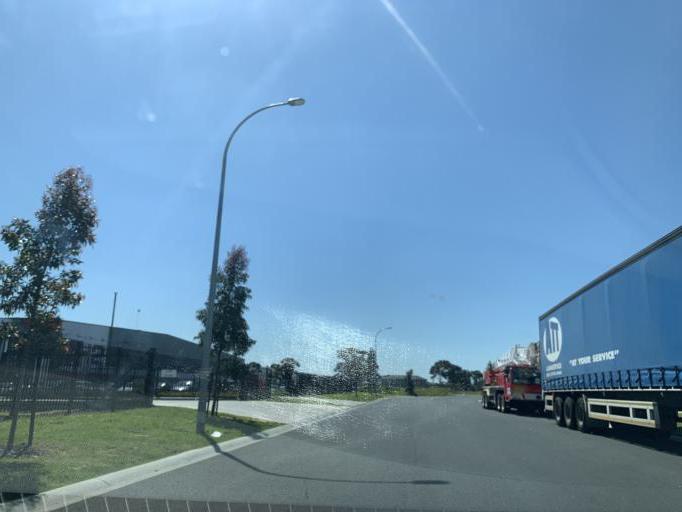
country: AU
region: Victoria
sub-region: Greater Dandenong
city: Keysborough
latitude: -38.0068
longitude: 145.1828
